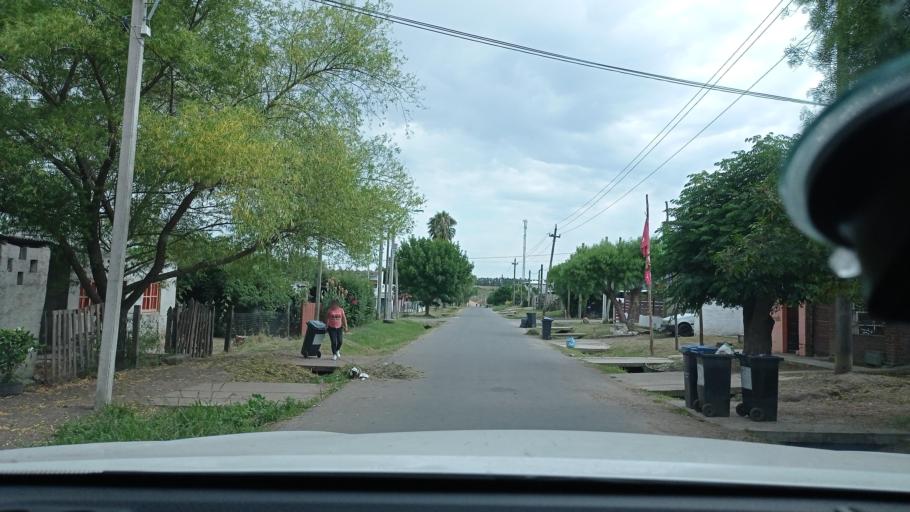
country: UY
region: Canelones
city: Pando
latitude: -34.7139
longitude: -55.9701
